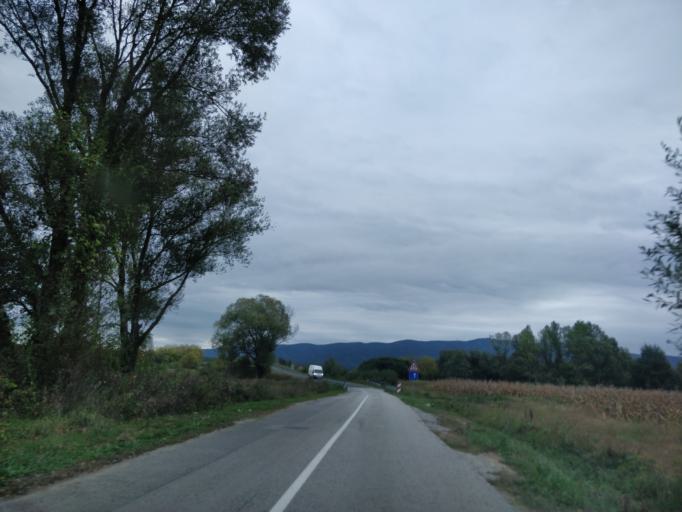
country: HR
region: Zagrebacka
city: Jakovlje
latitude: 45.9546
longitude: 15.8324
